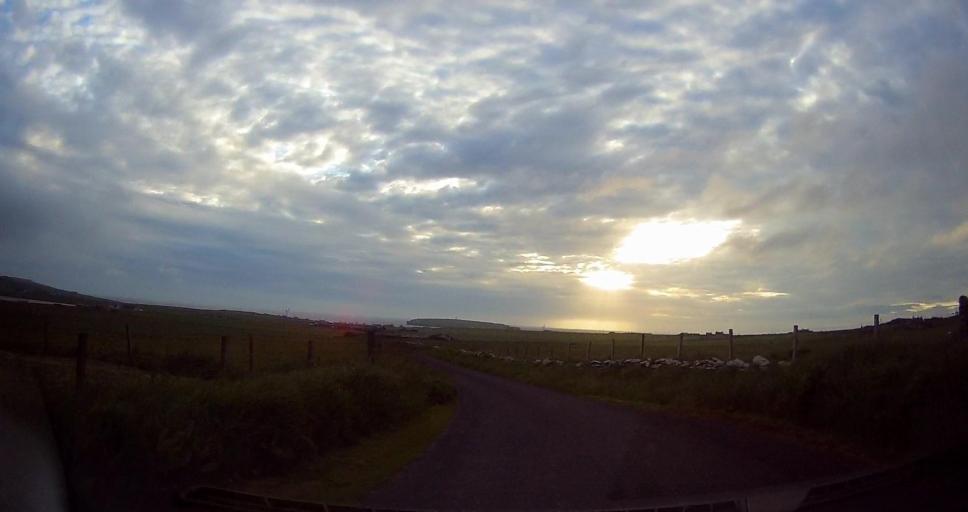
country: GB
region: Scotland
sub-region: Orkney Islands
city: Stromness
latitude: 59.1252
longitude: -3.2808
